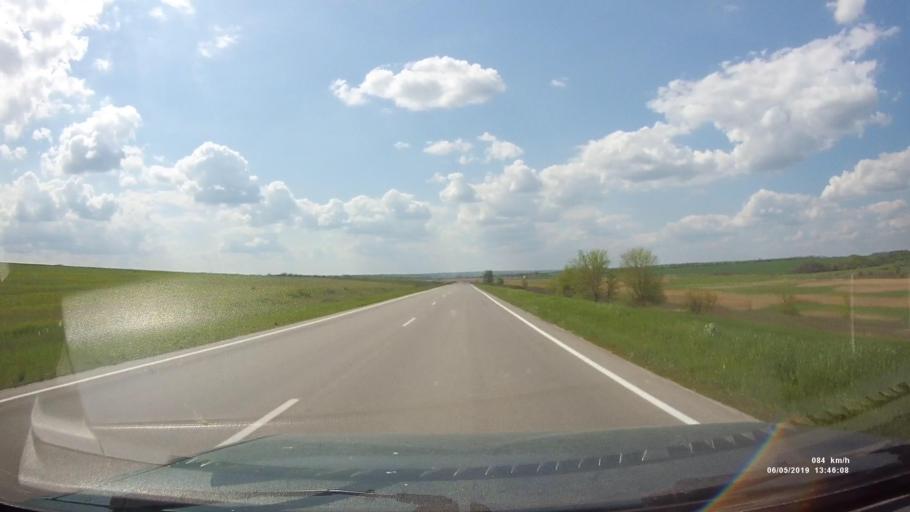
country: RU
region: Rostov
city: Melikhovskaya
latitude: 47.6578
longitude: 40.5874
